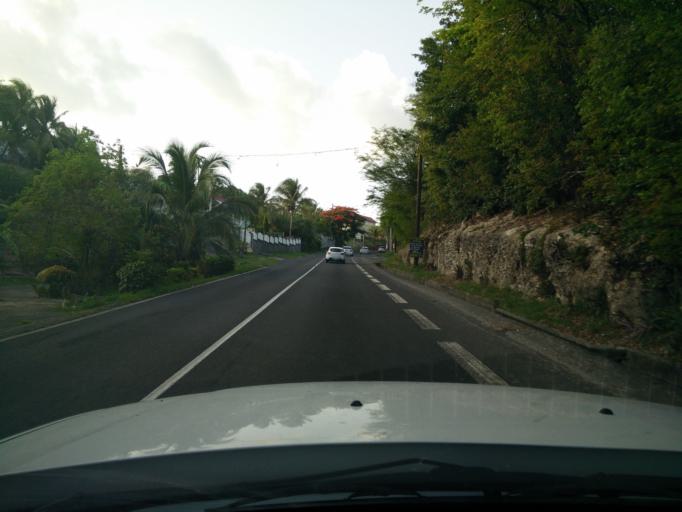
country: GP
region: Guadeloupe
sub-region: Guadeloupe
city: Le Gosier
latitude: 16.2098
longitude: -61.4418
